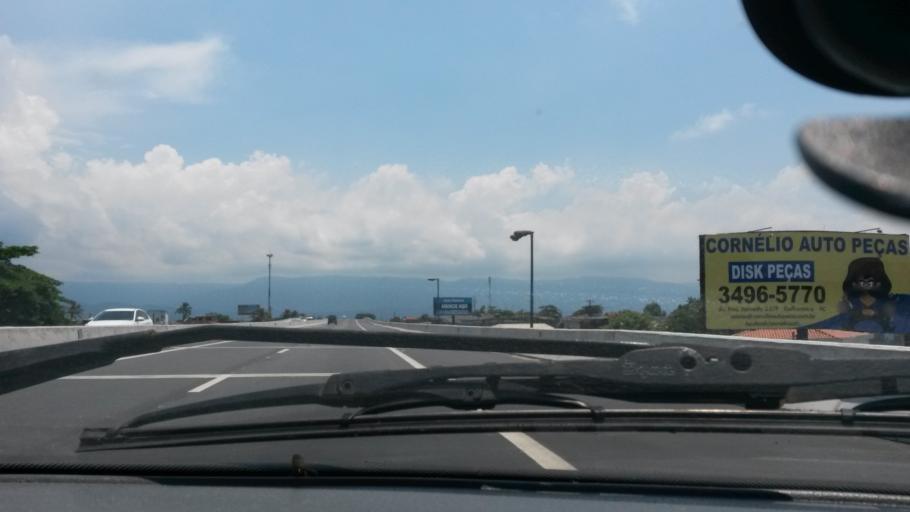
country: BR
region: Sao Paulo
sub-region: Sao Vicente
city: Sao Vicente
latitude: -23.9631
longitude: -46.4024
